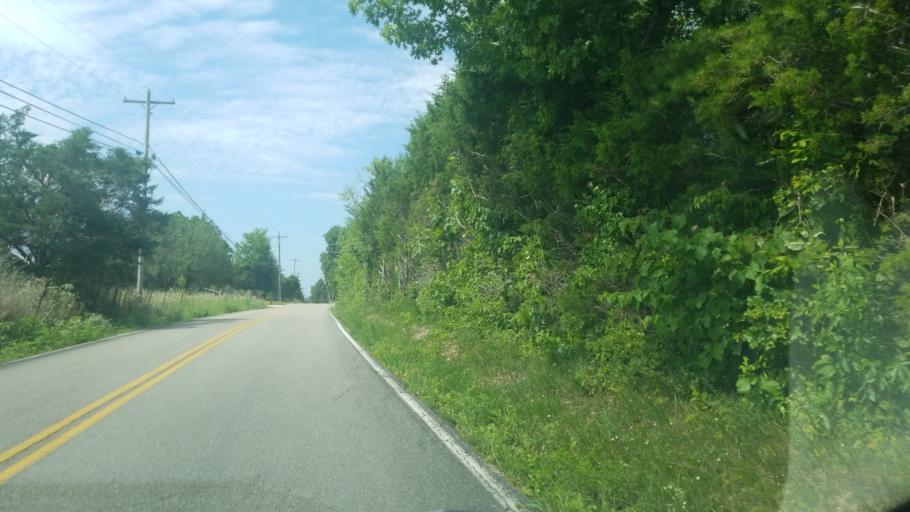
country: US
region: Tennessee
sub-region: Hamilton County
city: Lakesite
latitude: 35.2084
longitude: -85.0224
